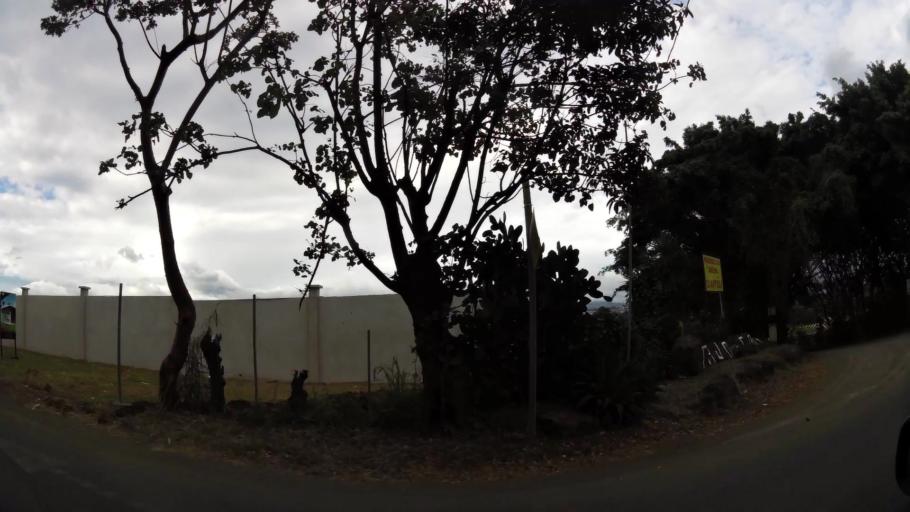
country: CR
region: Heredia
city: La Asuncion
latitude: 9.9597
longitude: -84.1719
